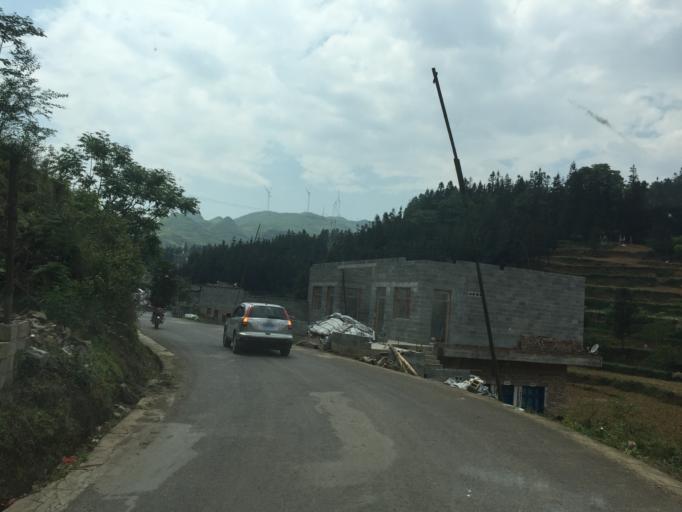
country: CN
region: Guangxi Zhuangzu Zizhiqu
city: Xinzhou
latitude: 25.6939
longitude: 105.2339
